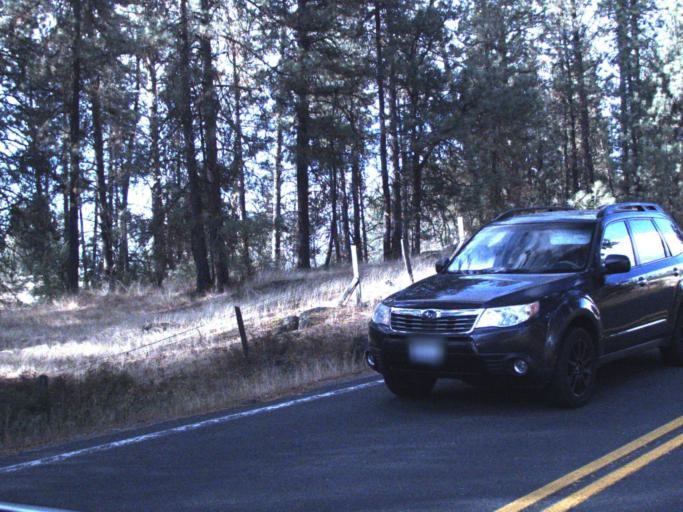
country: US
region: Washington
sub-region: Spokane County
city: Medical Lake
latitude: 47.5586
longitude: -117.6984
